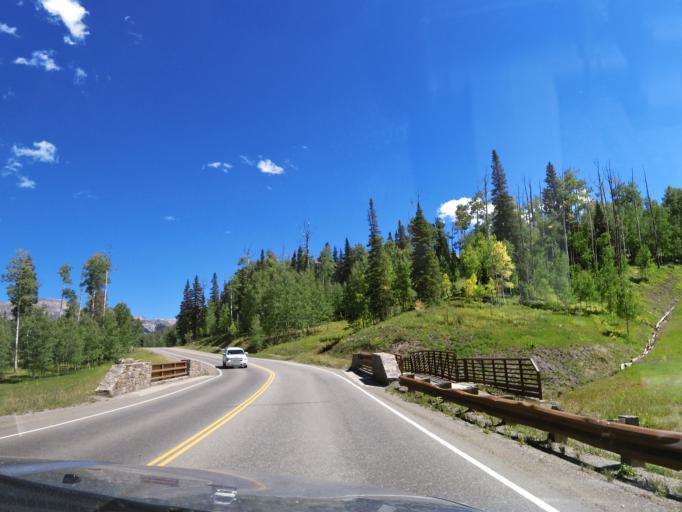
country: US
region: Colorado
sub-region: San Miguel County
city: Mountain Village
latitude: 37.9337
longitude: -107.8618
